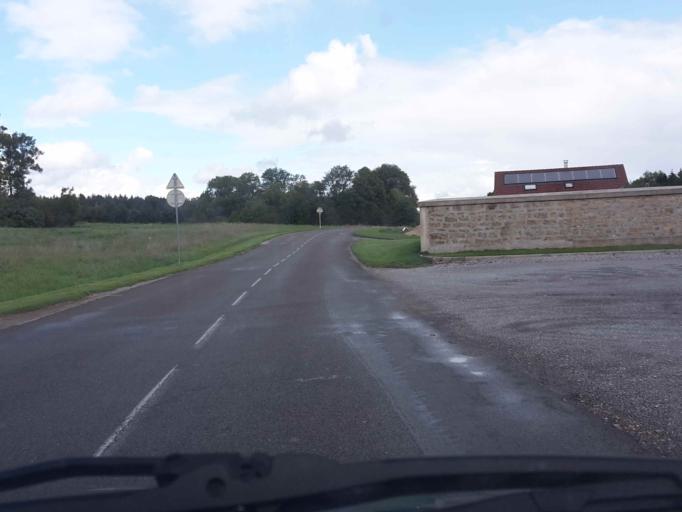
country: FR
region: Franche-Comte
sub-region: Departement du Doubs
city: Nancray
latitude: 47.2691
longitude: 6.2161
